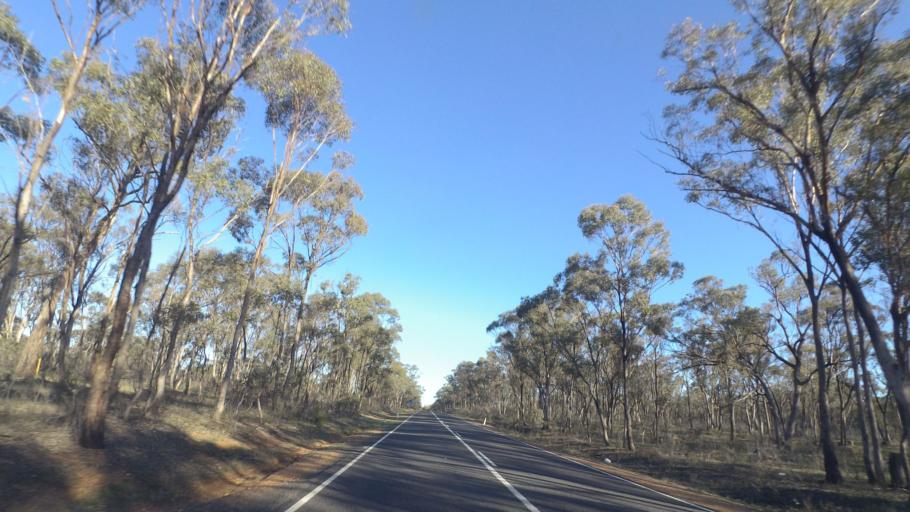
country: AU
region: Victoria
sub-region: Greater Bendigo
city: Kennington
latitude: -36.8872
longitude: 144.4931
